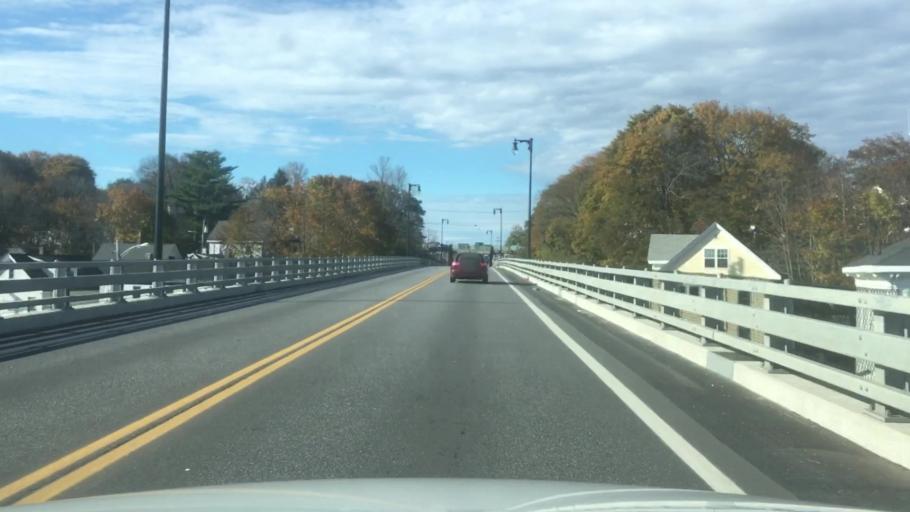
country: US
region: Maine
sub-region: Sagadahoc County
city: Bath
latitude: 43.9112
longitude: -69.8174
